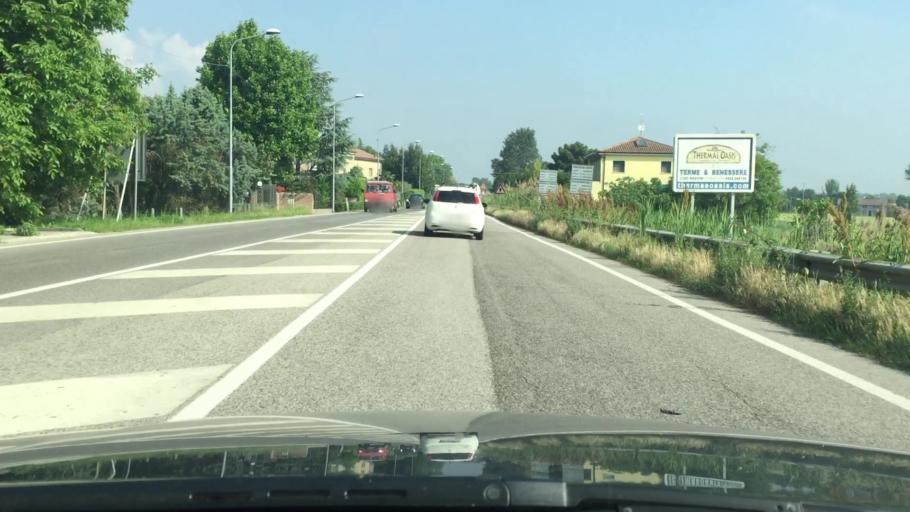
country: IT
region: Emilia-Romagna
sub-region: Provincia di Ferrara
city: Pontegradella
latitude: 44.8071
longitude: 11.6359
